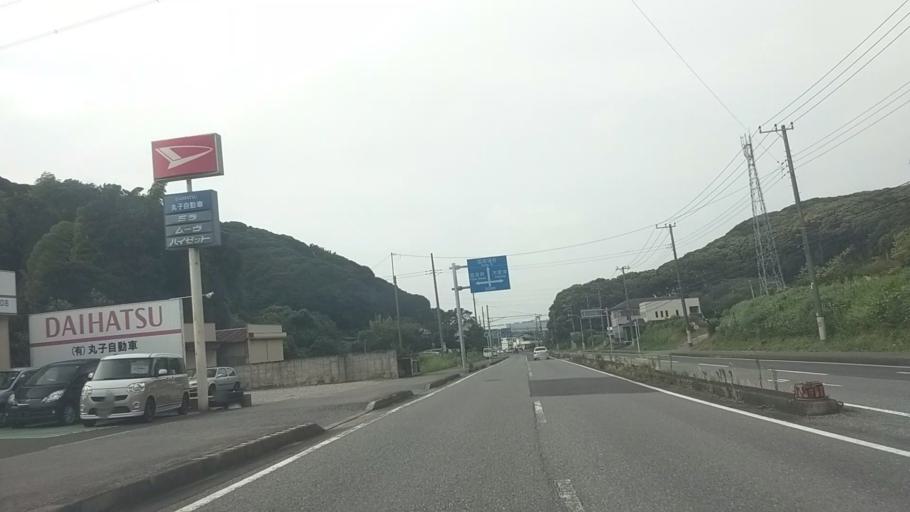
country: JP
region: Chiba
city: Kimitsu
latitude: 35.3439
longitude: 139.8903
